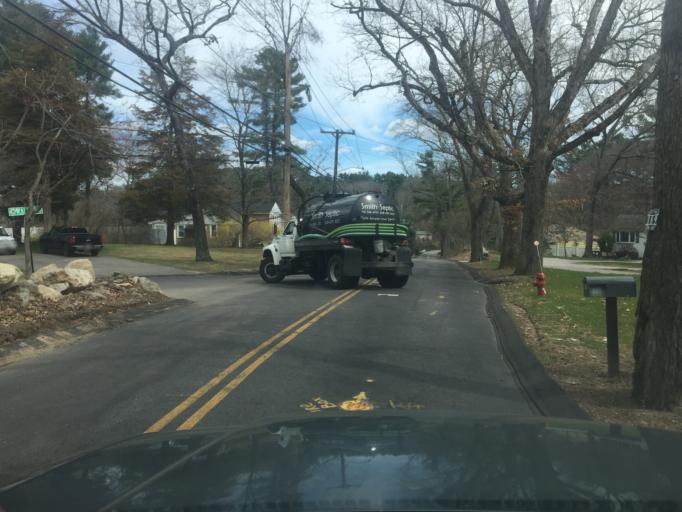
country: US
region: Massachusetts
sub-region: Norfolk County
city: Millis
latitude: 42.1848
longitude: -71.3784
